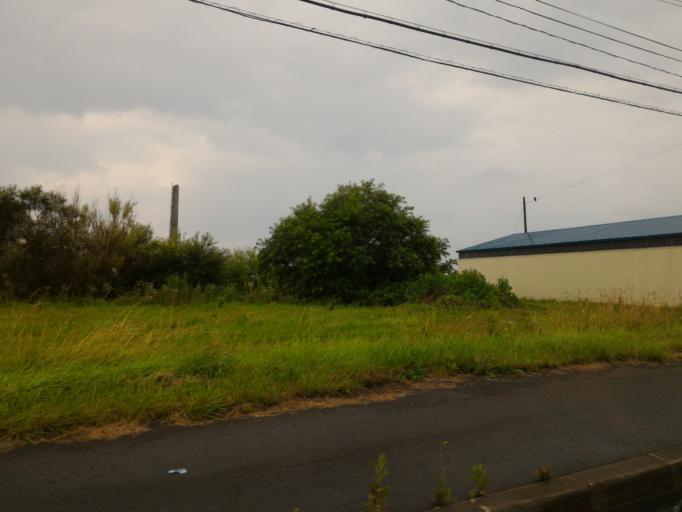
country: JP
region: Hokkaido
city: Rumoi
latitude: 43.9547
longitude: 141.6443
